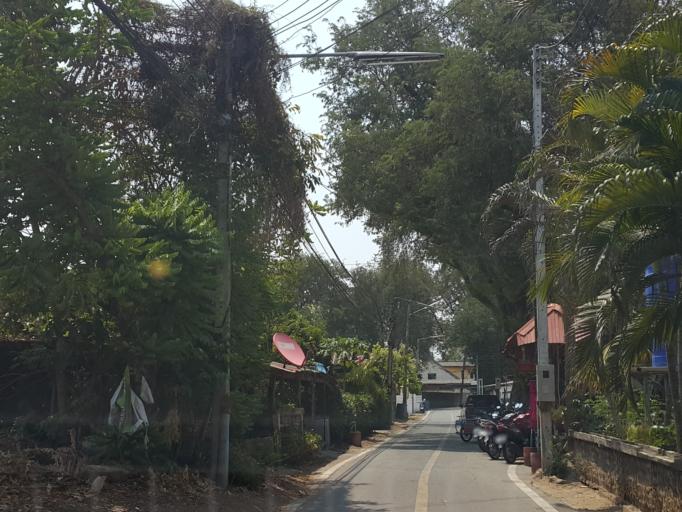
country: TH
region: Kanchanaburi
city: Kanchanaburi
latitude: 14.0301
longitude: 99.5225
